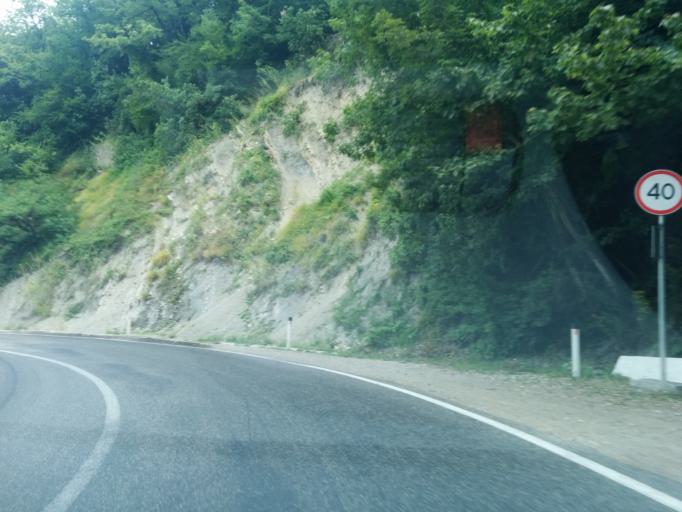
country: RU
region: Krasnodarskiy
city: Agoy
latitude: 44.1430
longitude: 39.0563
